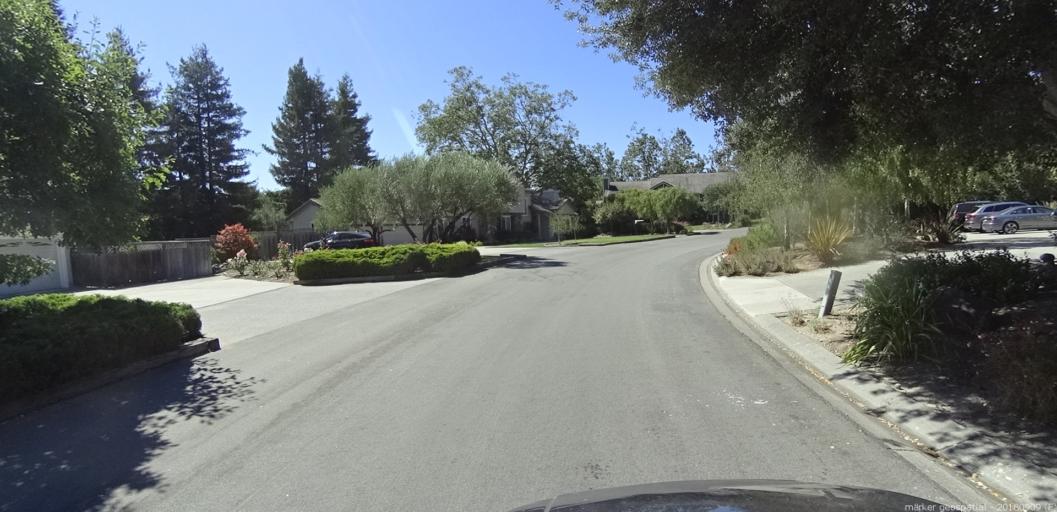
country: US
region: California
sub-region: Monterey County
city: Salinas
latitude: 36.6042
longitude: -121.7010
